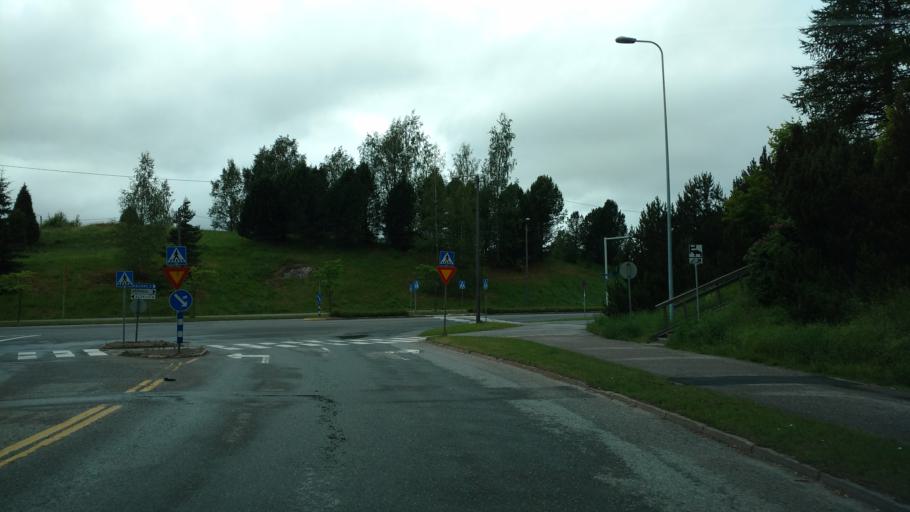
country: FI
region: Varsinais-Suomi
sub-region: Salo
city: Salo
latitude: 60.3936
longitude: 23.1092
